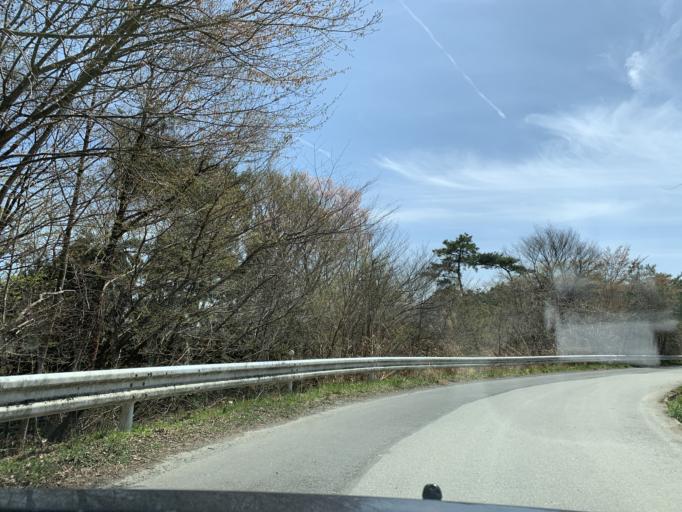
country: JP
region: Iwate
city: Ichinoseki
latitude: 38.8162
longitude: 141.2741
